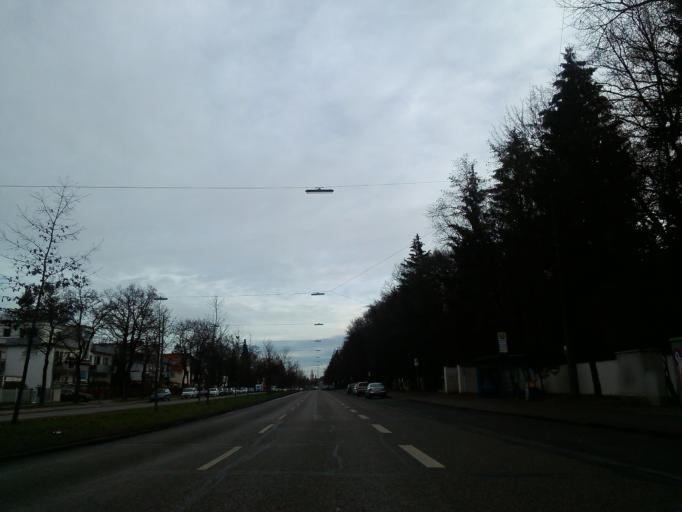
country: DE
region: Bavaria
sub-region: Upper Bavaria
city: Neuried
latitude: 48.1121
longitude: 11.4951
